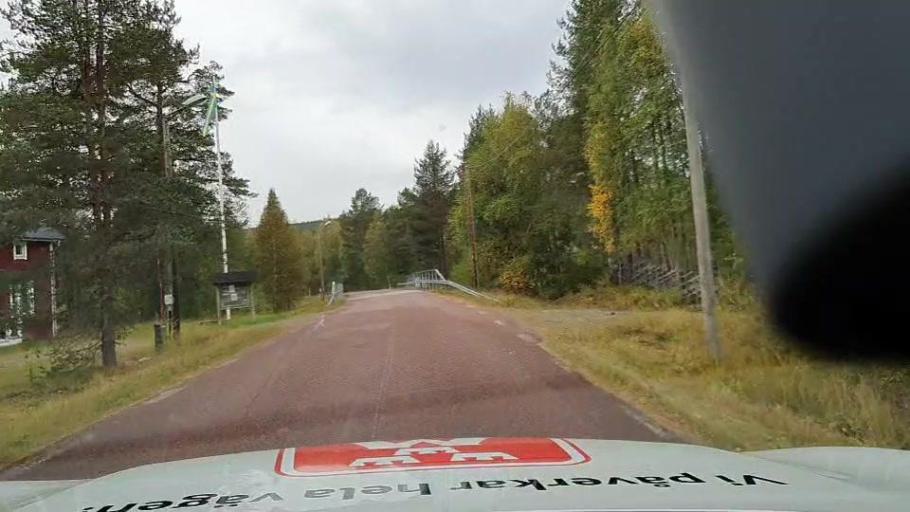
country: NO
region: Hedmark
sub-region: Engerdal
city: Engerdal
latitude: 62.0108
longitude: 12.6652
